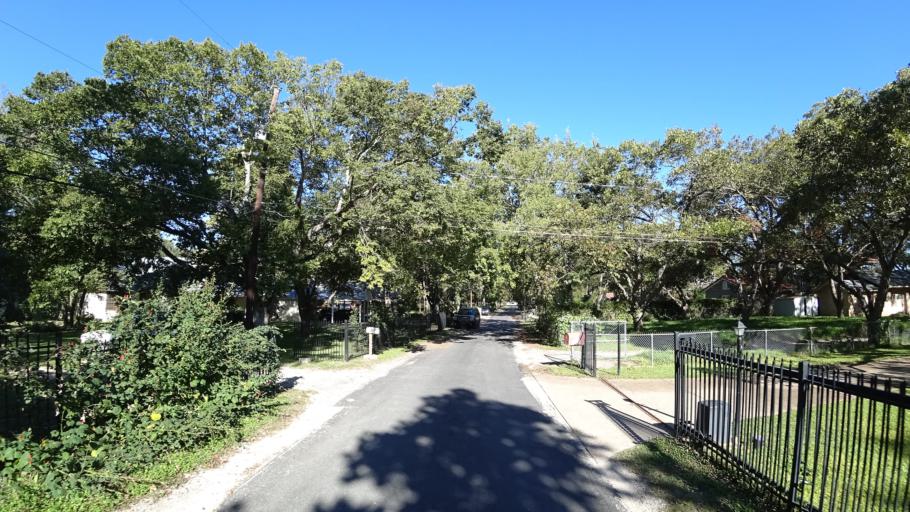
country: US
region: Texas
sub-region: Travis County
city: West Lake Hills
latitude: 30.3422
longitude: -97.7895
